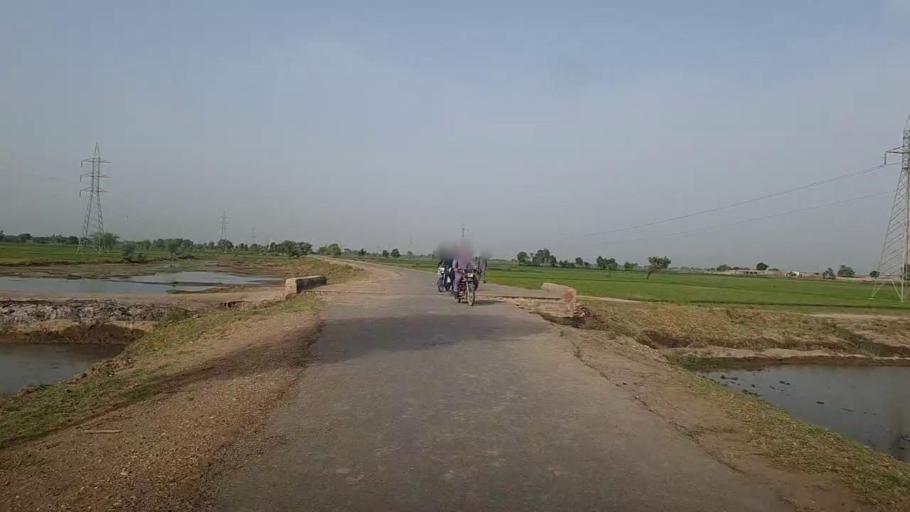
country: PK
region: Sindh
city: Mehar
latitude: 27.1410
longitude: 67.7933
